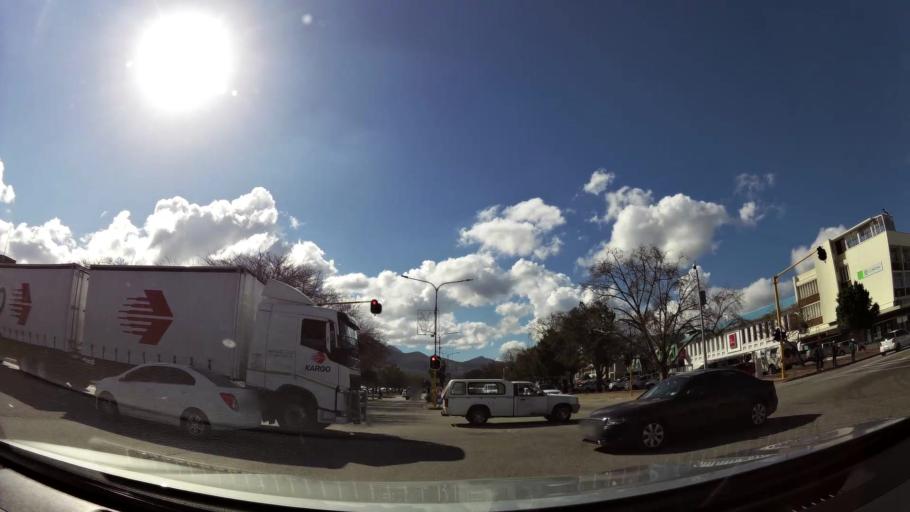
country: ZA
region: Western Cape
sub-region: Eden District Municipality
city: George
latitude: -33.9588
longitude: 22.4567
